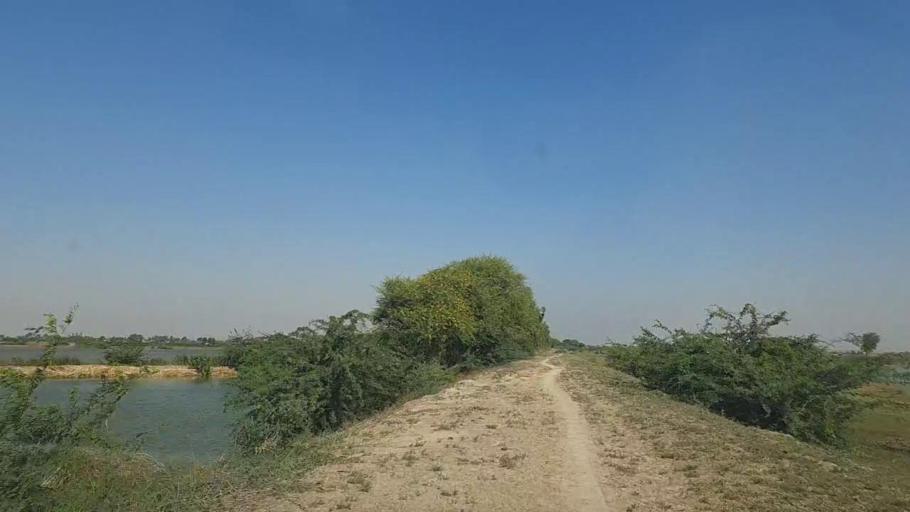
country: PK
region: Sindh
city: Thatta
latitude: 24.8005
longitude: 67.9811
